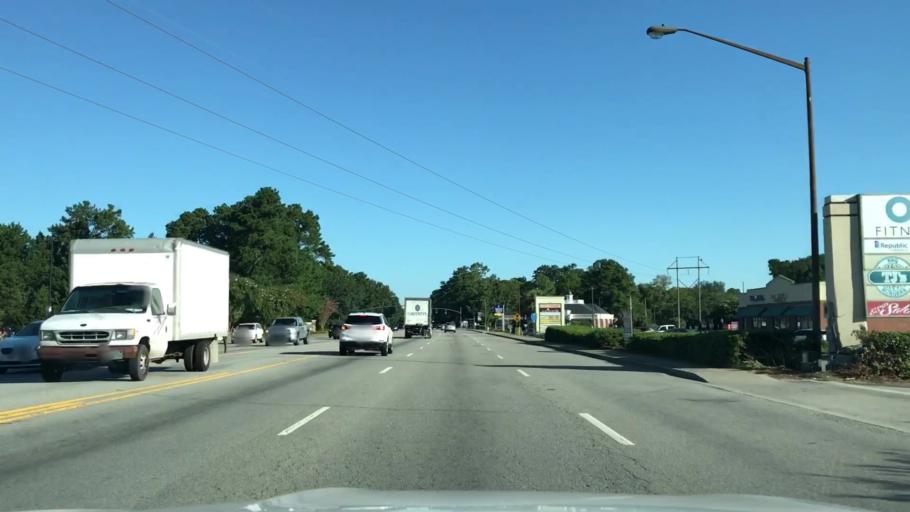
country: US
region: South Carolina
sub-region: Berkeley County
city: Goose Creek
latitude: 33.0082
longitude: -80.0452
